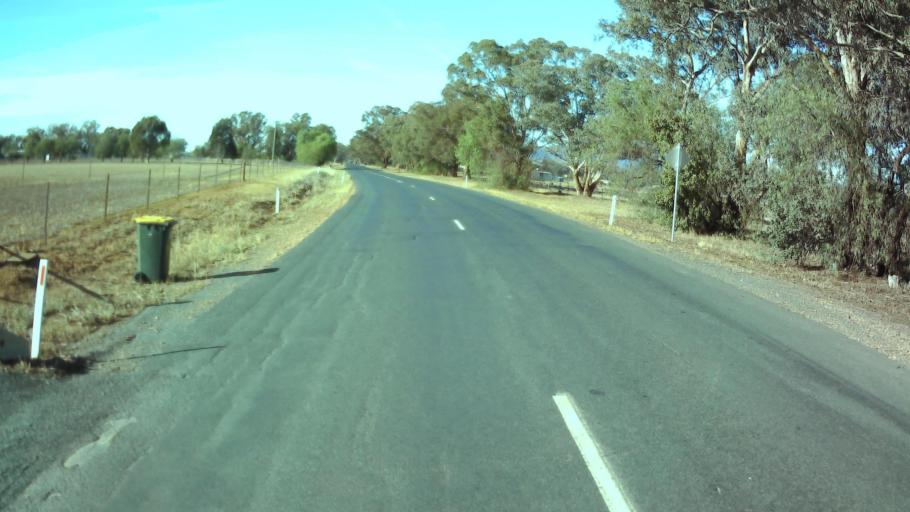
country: AU
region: New South Wales
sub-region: Weddin
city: Grenfell
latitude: -33.9075
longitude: 148.1462
